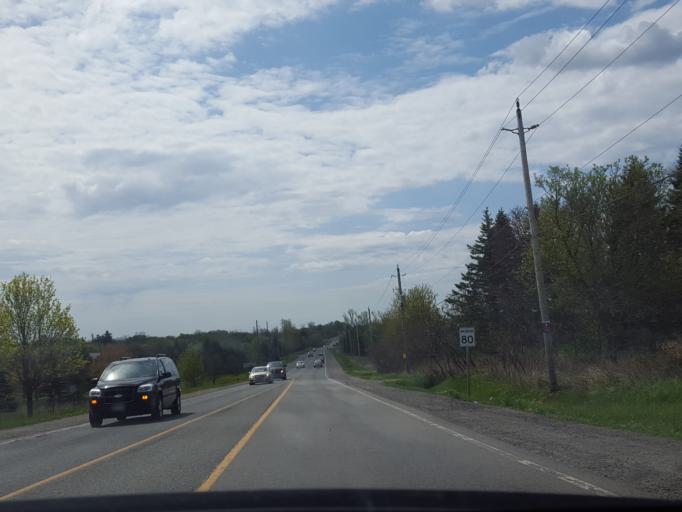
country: CA
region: Ontario
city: Oshawa
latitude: 43.9212
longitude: -78.7064
